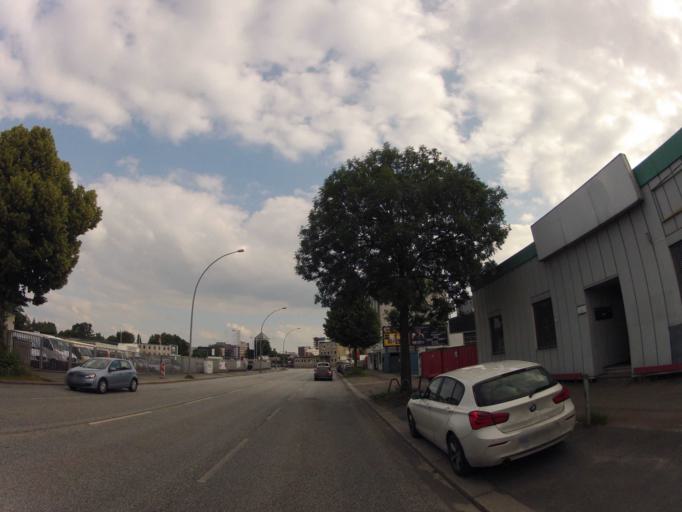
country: DE
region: Hamburg
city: Hammerbrook
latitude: 53.5452
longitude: 10.0404
